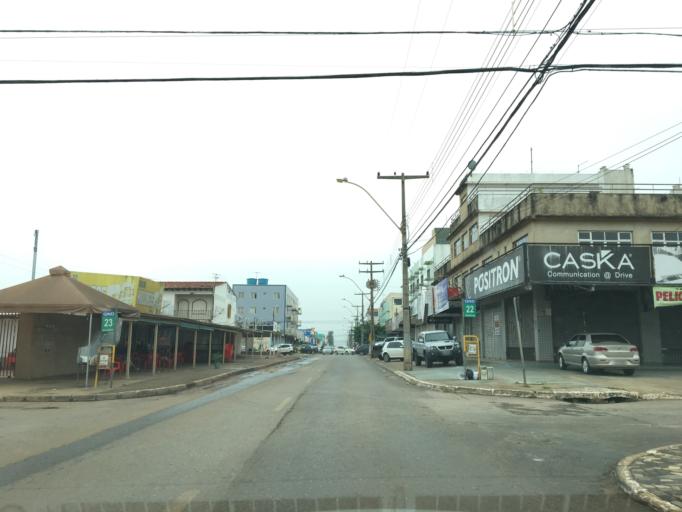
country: BR
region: Federal District
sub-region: Brasilia
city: Brasilia
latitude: -15.8104
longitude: -48.0606
